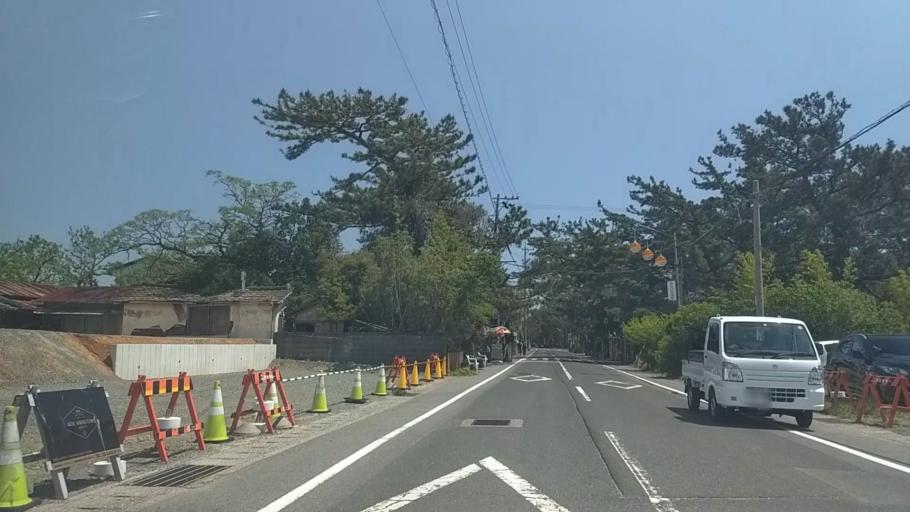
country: JP
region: Shizuoka
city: Kosai-shi
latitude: 34.6839
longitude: 137.5856
